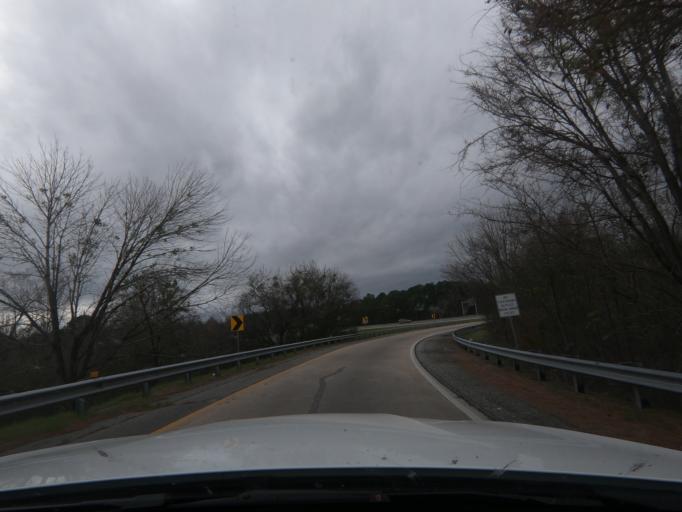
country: US
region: Alabama
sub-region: Russell County
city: Phenix City
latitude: 32.5433
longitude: -84.9590
